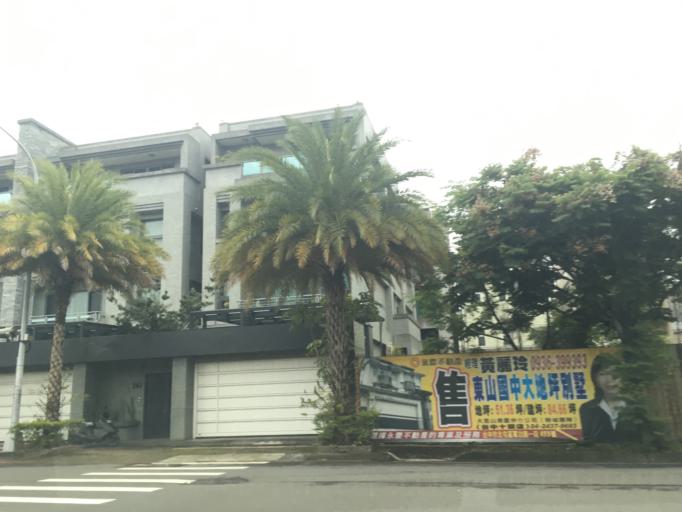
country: TW
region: Taiwan
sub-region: Taichung City
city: Taichung
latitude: 24.1674
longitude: 120.7158
